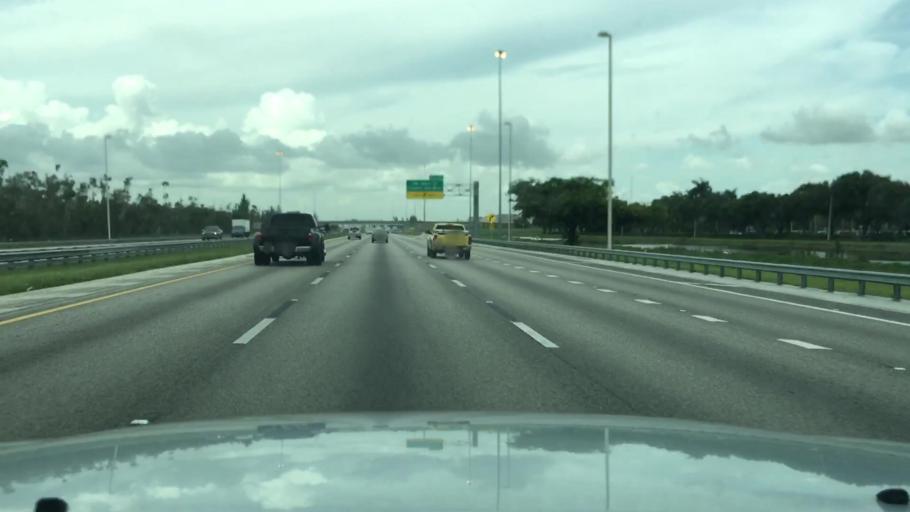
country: US
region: Florida
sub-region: Miami-Dade County
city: Doral
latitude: 25.8591
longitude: -80.3935
